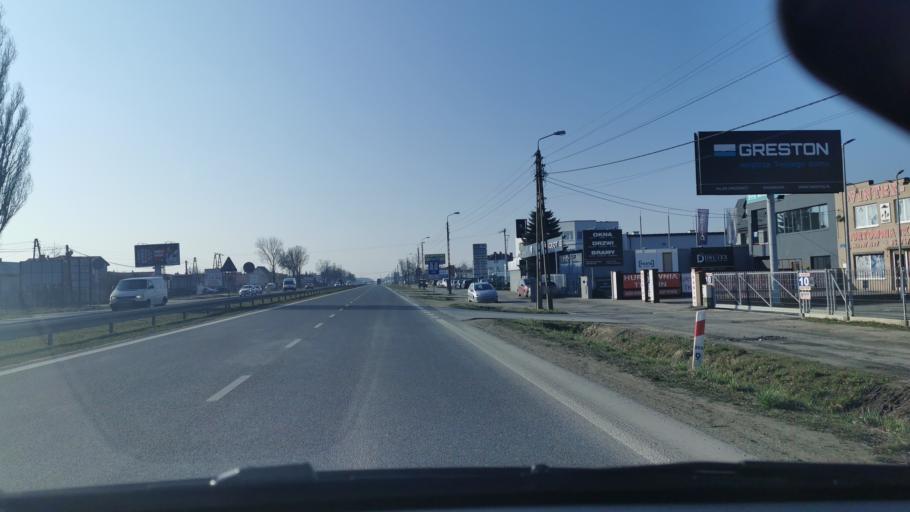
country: PL
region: Masovian Voivodeship
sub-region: Powiat pruszkowski
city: Nowe Grocholice
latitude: 52.1225
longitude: 20.8940
